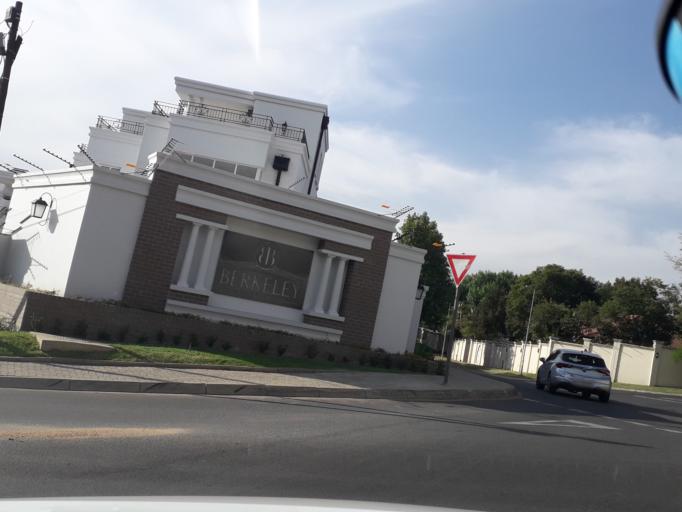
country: ZA
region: Gauteng
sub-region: City of Johannesburg Metropolitan Municipality
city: Diepsloot
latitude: -26.0593
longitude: 28.0194
